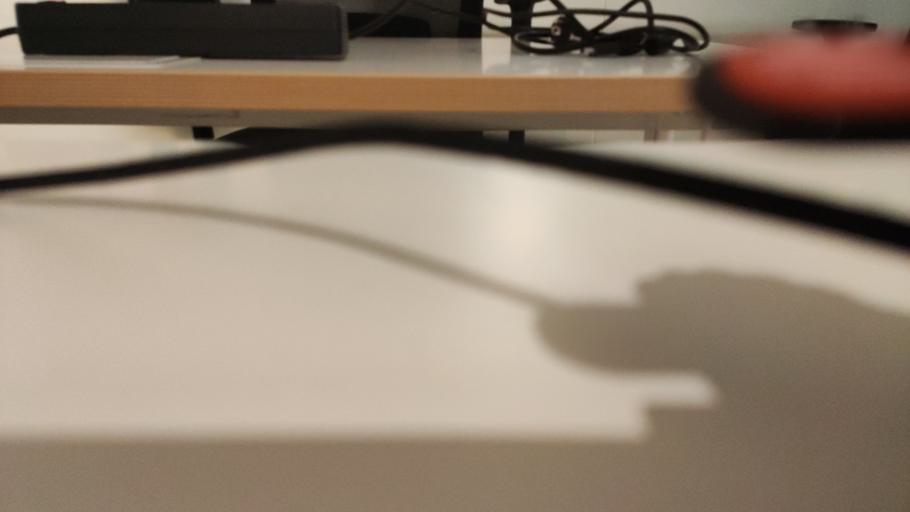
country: RU
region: Moskovskaya
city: Proletarskiy
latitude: 54.9757
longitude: 37.4048
